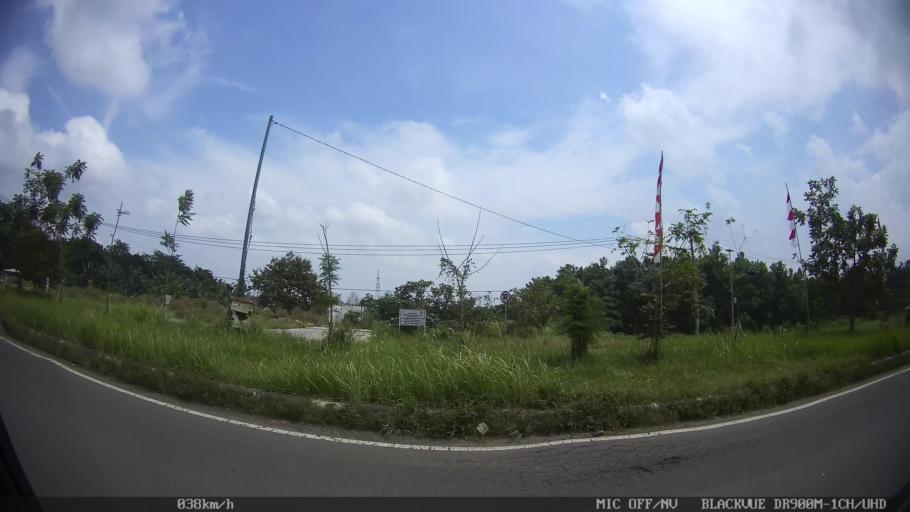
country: ID
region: Lampung
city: Kedaton
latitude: -5.3585
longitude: 105.3070
